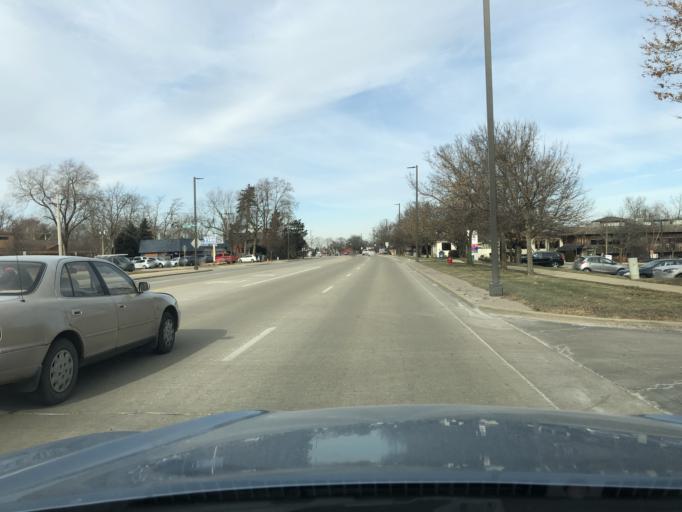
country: US
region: Illinois
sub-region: Cook County
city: Wheeling
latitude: 42.1332
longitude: -87.9020
